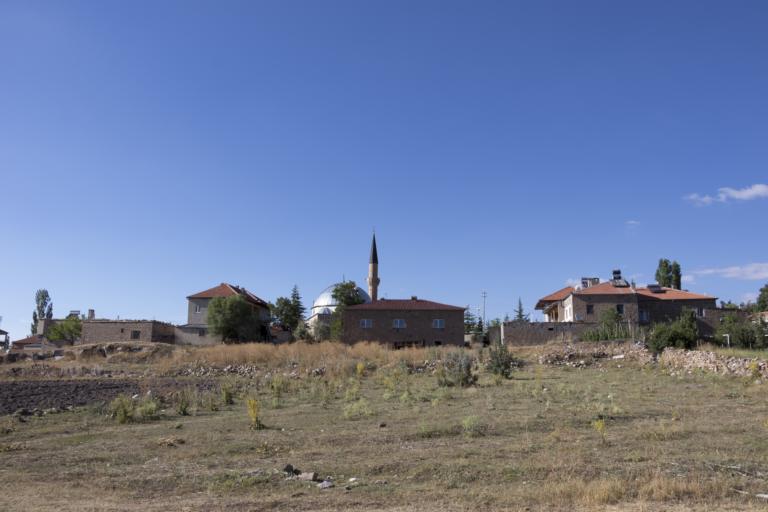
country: TR
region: Kayseri
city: Toklar
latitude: 38.4050
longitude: 36.0819
